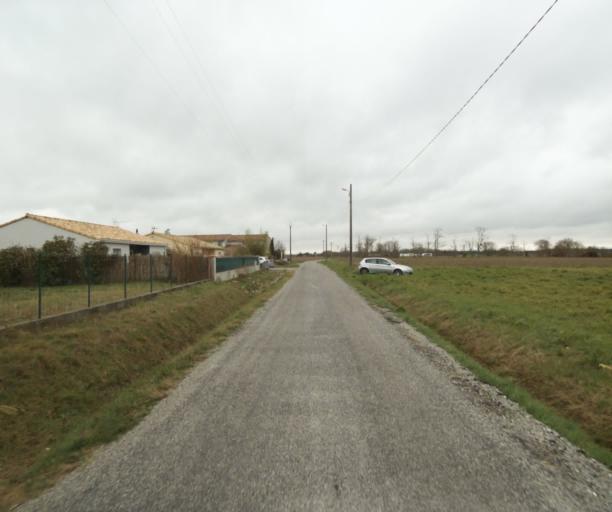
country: FR
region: Midi-Pyrenees
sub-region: Departement de l'Ariege
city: Mazeres
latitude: 43.2399
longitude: 1.6801
